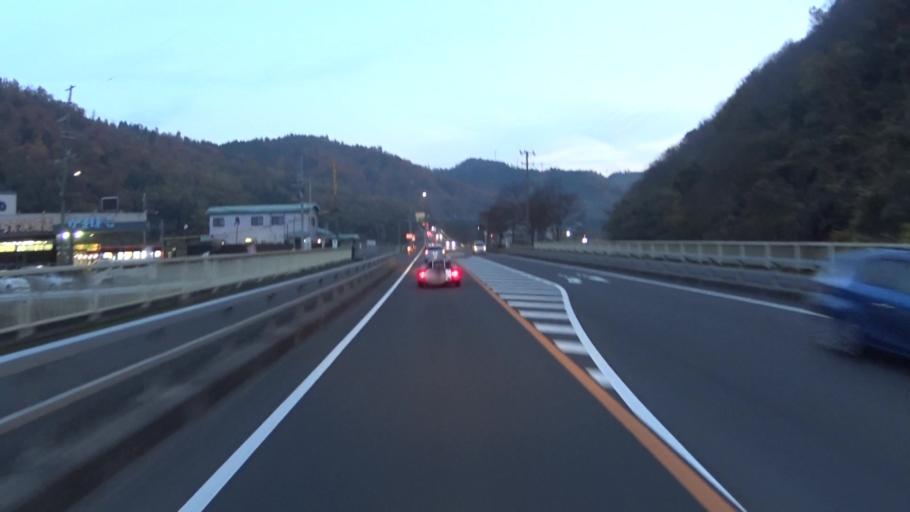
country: JP
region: Kyoto
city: Maizuru
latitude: 35.4190
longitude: 135.3310
